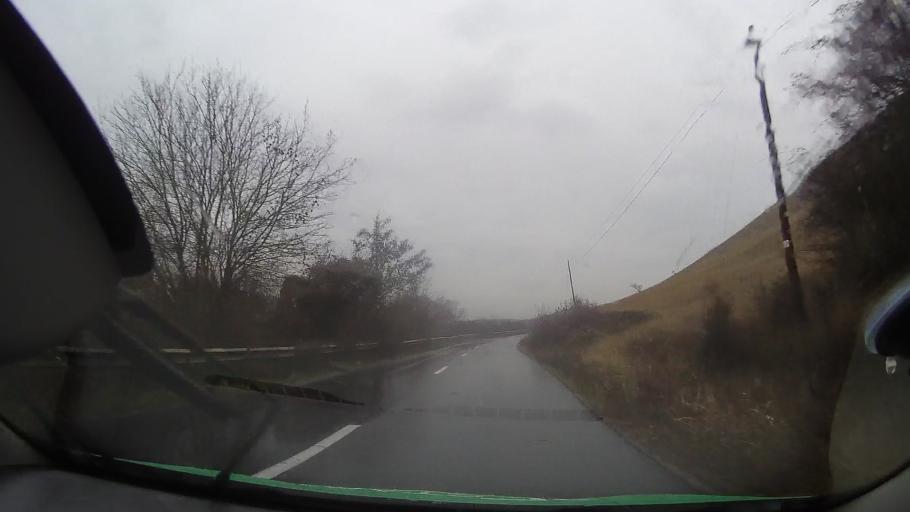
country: RO
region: Bihor
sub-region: Comuna Pocola
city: Pocola
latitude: 46.6798
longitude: 22.2537
